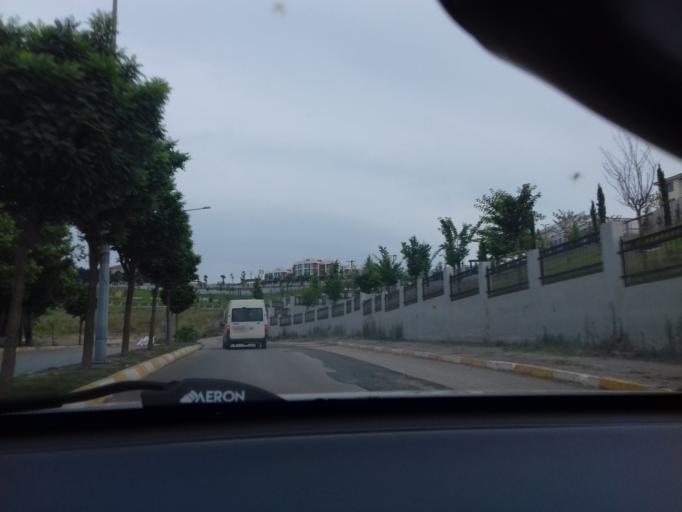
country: TR
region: Istanbul
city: Sultanbeyli
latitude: 40.9328
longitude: 29.3021
